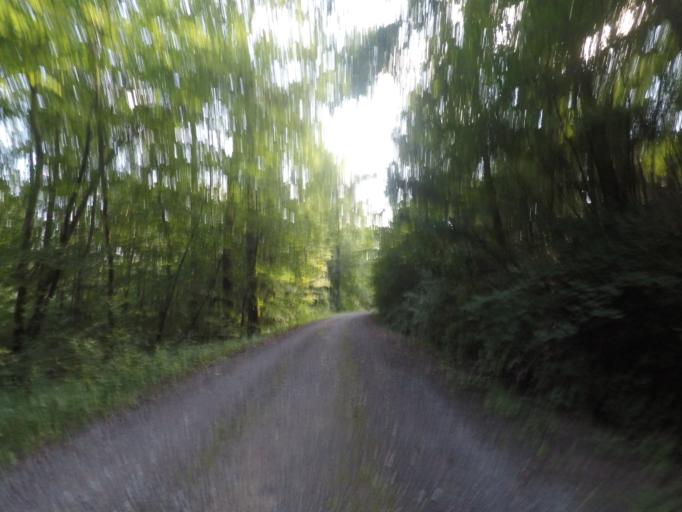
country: DE
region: Baden-Wuerttemberg
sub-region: Regierungsbezirk Stuttgart
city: Steinenbronn
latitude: 48.6690
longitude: 9.0984
